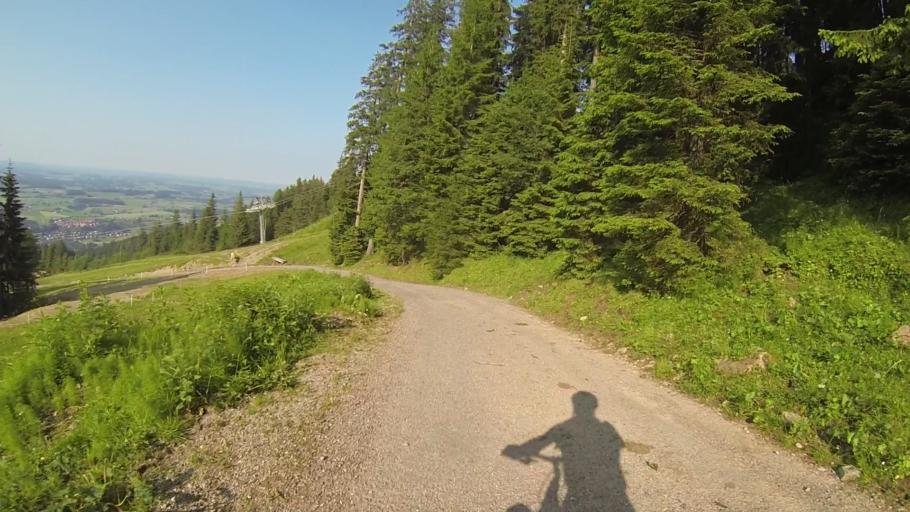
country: DE
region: Bavaria
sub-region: Swabia
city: Nesselwang
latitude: 47.6023
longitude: 10.4979
